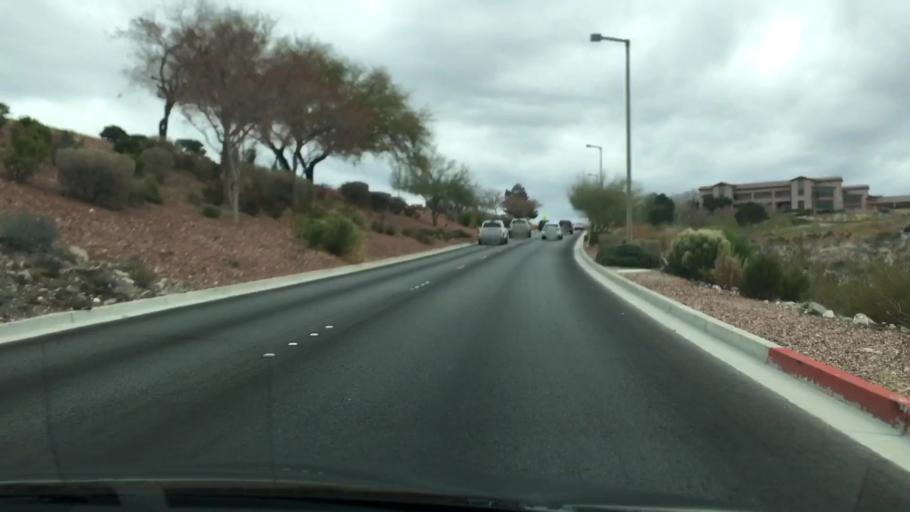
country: US
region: Nevada
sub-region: Clark County
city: Whitney
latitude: 35.9598
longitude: -115.0953
